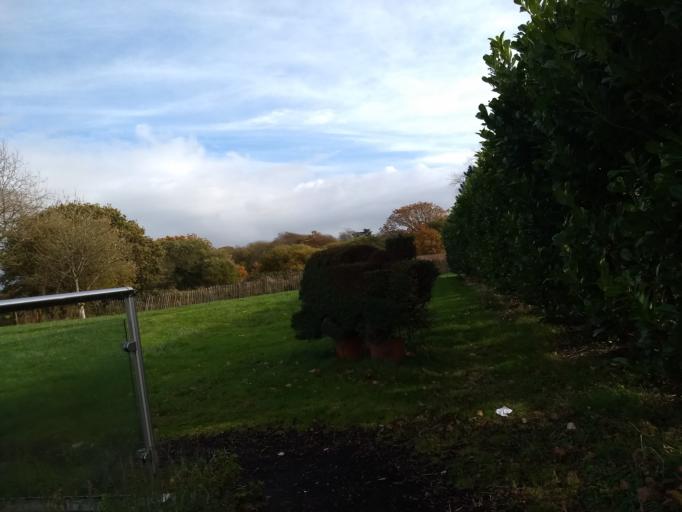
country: GB
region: England
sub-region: Isle of Wight
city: Freshwater
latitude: 50.6815
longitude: -1.5142
